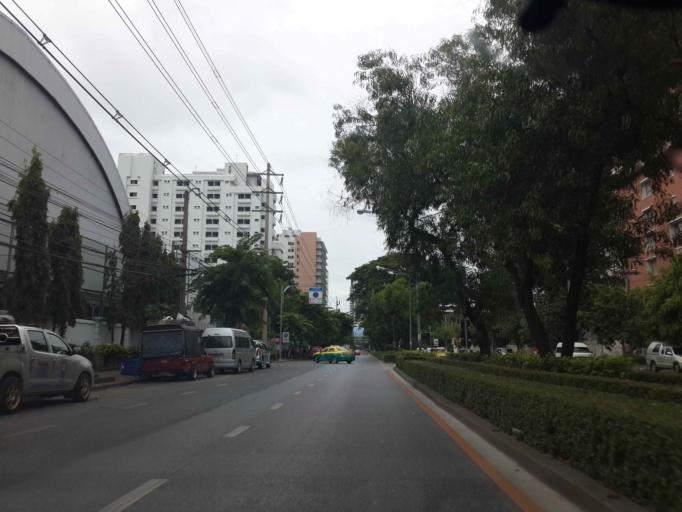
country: TH
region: Bangkok
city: Pathum Wan
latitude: 13.7371
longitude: 100.5346
